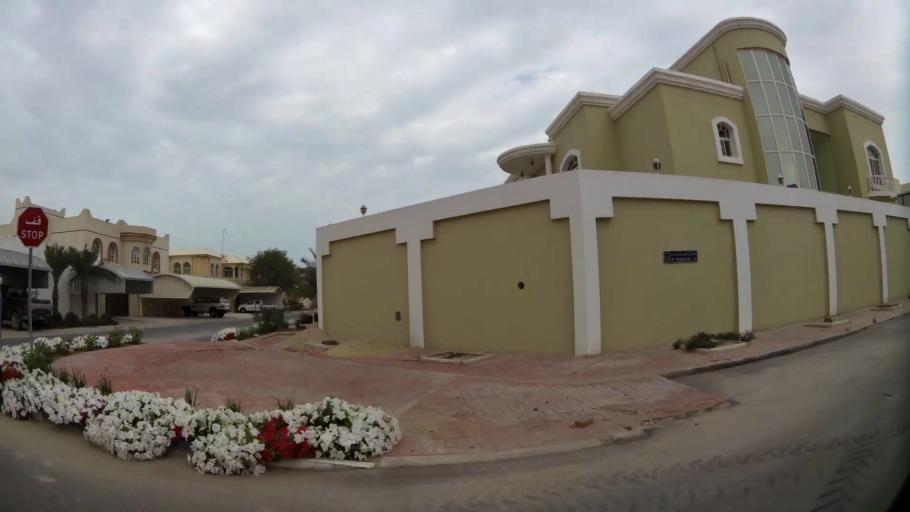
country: QA
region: Baladiyat ar Rayyan
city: Ar Rayyan
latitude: 25.3409
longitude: 51.4608
